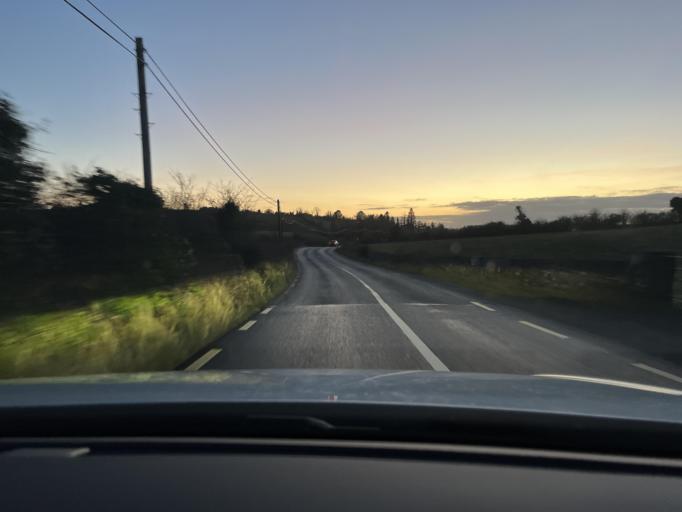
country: IE
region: Connaught
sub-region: County Leitrim
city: Carrick-on-Shannon
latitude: 53.9843
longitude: -8.0446
